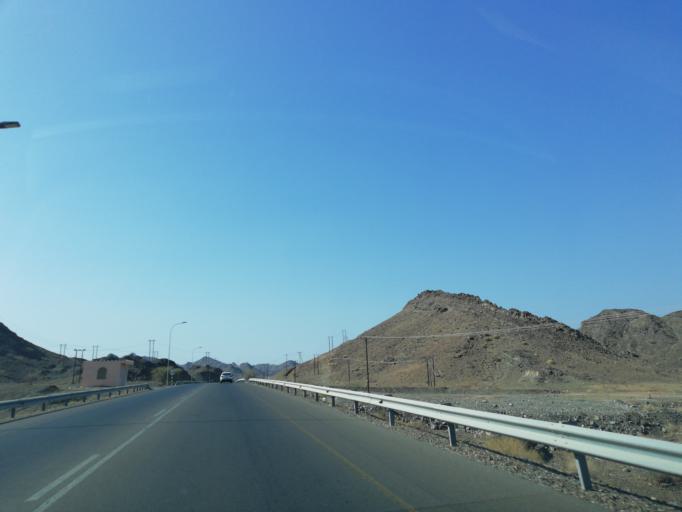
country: OM
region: Ash Sharqiyah
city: Ibra'
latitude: 22.8138
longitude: 58.1681
